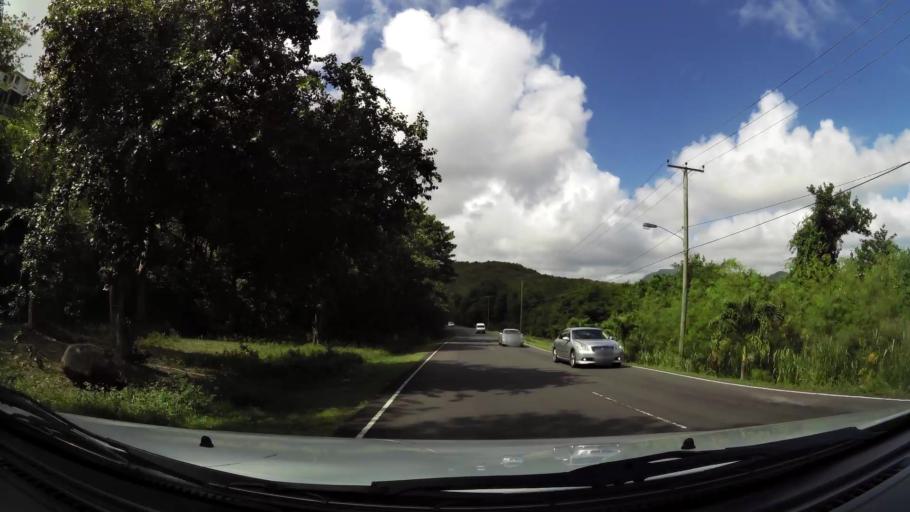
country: LC
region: Dennery Quarter
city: Dennery
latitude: 13.9190
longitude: -60.8943
